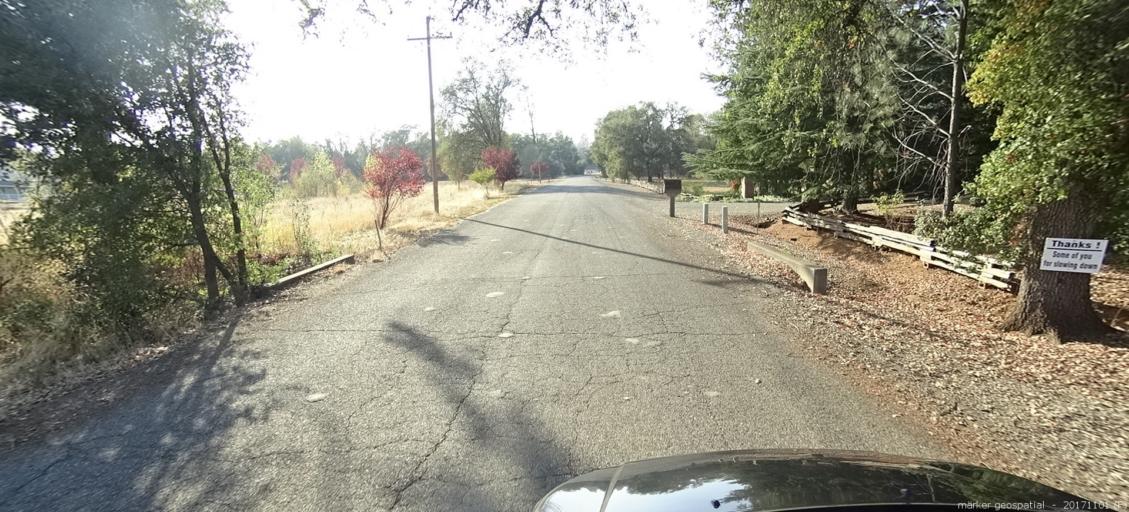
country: US
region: California
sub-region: Shasta County
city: Shasta Lake
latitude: 40.6197
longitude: -122.3141
